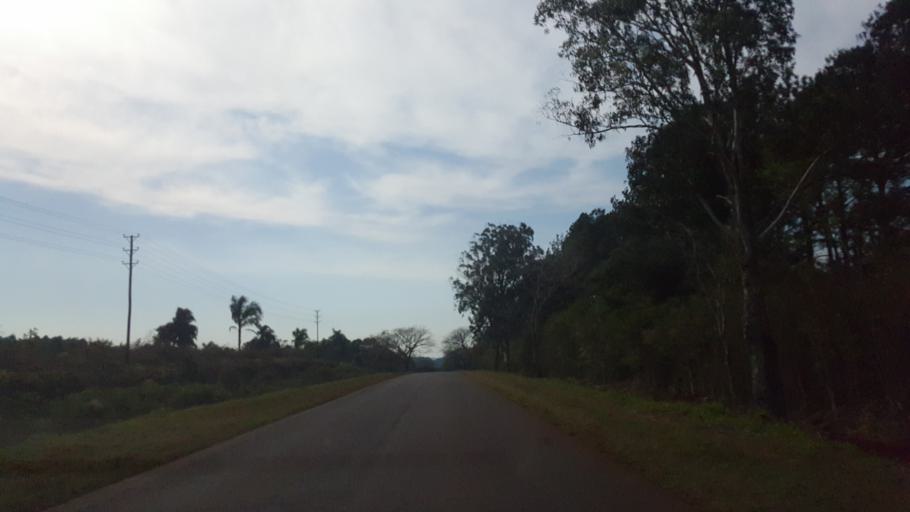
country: AR
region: Misiones
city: Capiovi
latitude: -26.9332
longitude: -55.0915
